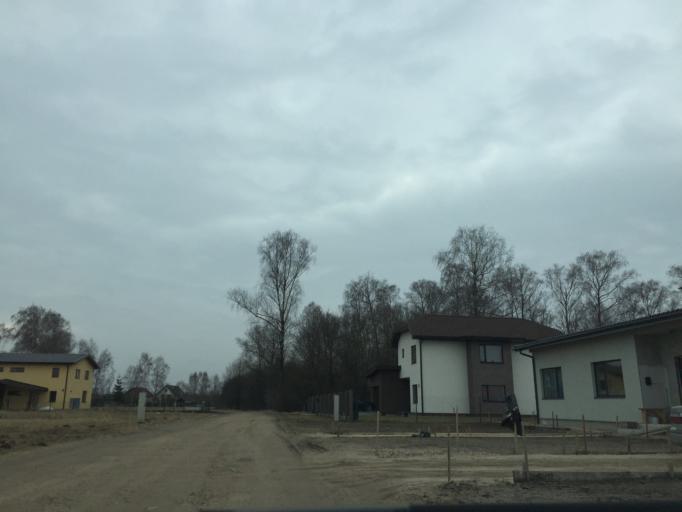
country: LV
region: Marupe
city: Marupe
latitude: 56.8819
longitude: 24.0550
